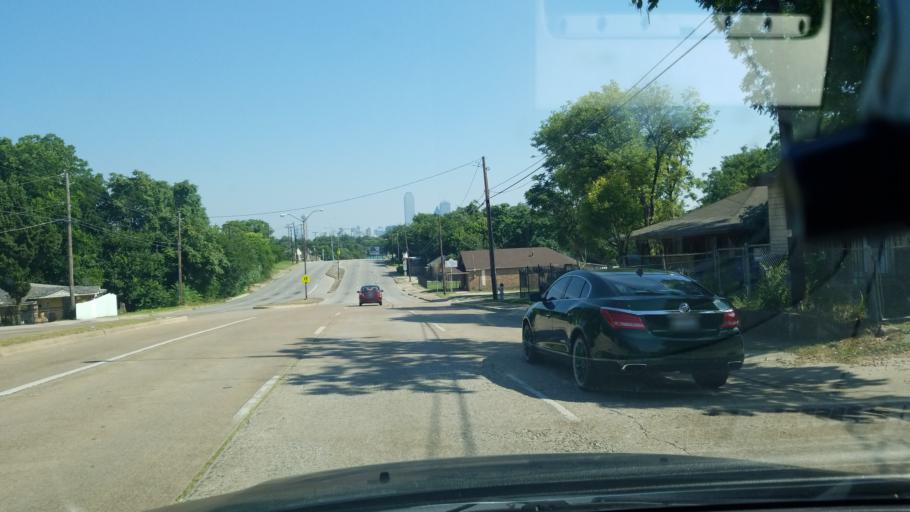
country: US
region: Texas
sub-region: Dallas County
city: Dallas
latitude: 32.7429
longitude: -96.7987
